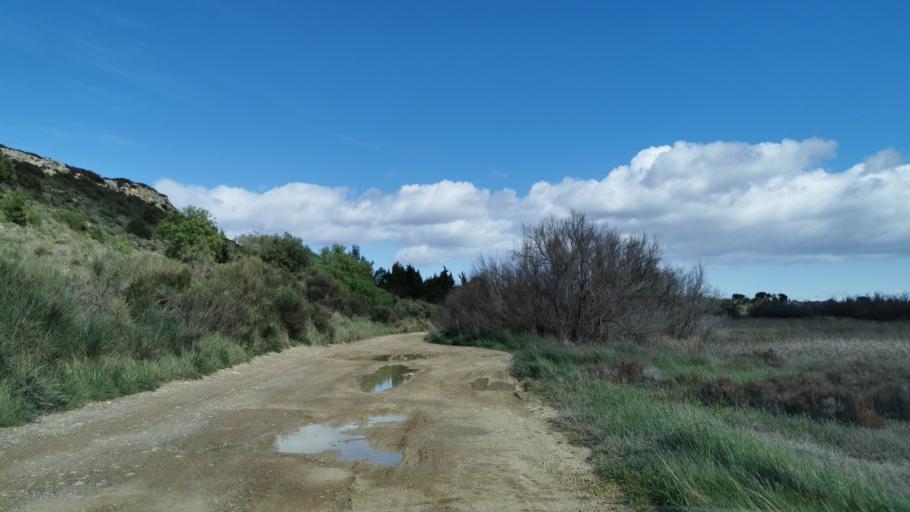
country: FR
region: Languedoc-Roussillon
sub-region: Departement de l'Aude
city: Narbonne
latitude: 43.1484
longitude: 2.9862
